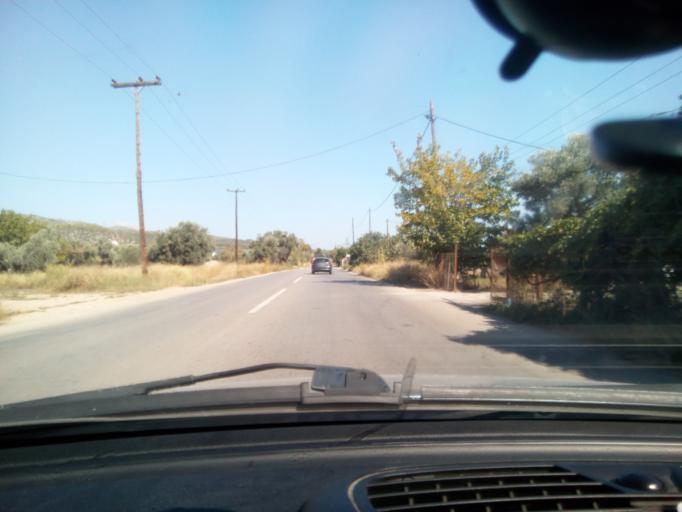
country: GR
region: Central Greece
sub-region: Nomos Evvoias
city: Filla
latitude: 38.4160
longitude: 23.7035
